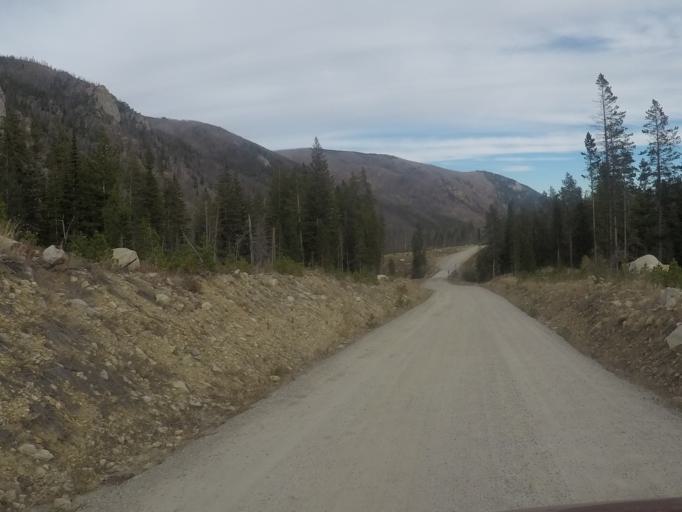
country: US
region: Montana
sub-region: Carbon County
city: Red Lodge
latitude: 45.1734
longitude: -109.4370
